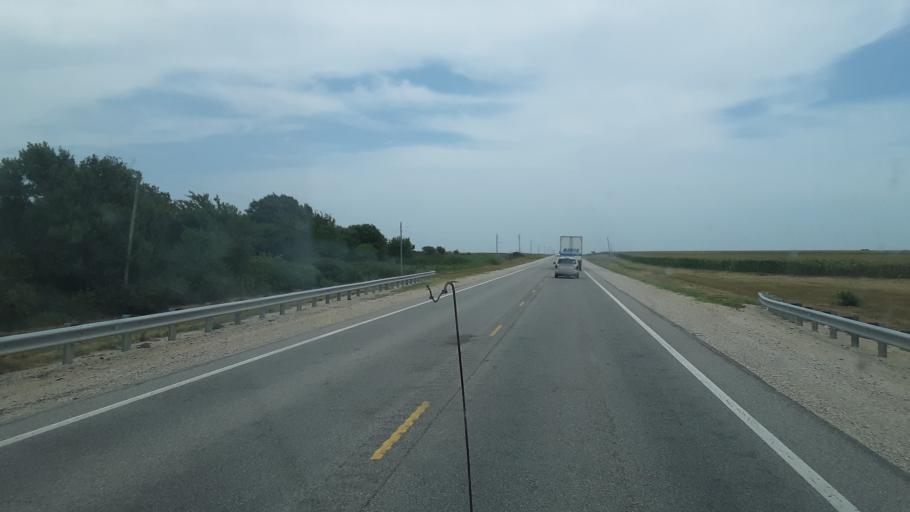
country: US
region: Kansas
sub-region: Allen County
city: Iola
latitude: 37.9218
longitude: -95.2577
